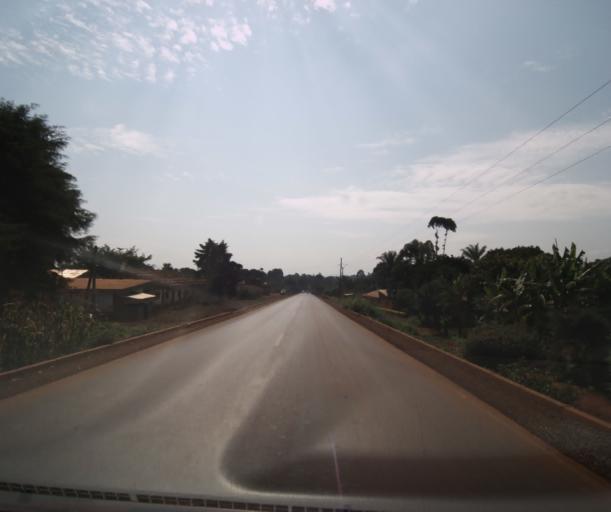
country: CM
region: West
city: Mbouda
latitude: 5.6191
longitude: 10.2753
